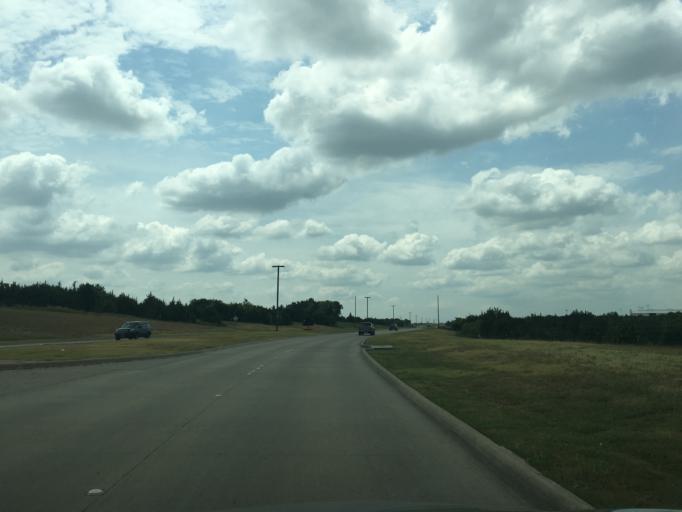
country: US
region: Texas
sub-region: Rockwall County
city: Rockwall
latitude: 32.9326
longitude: -96.4384
